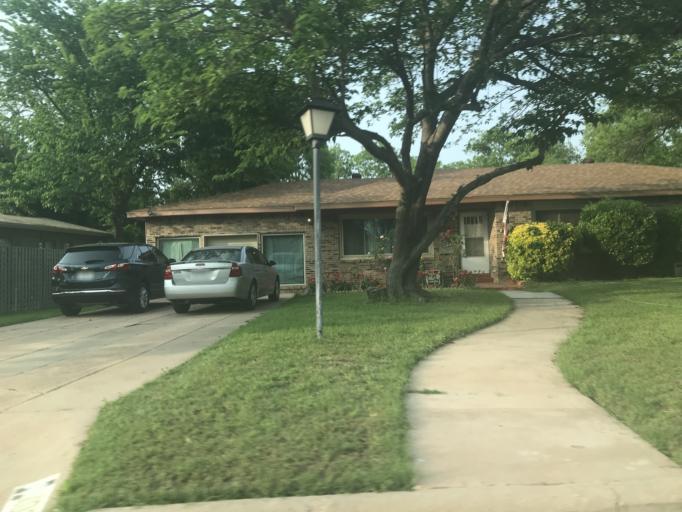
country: US
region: Texas
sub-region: Taylor County
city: Abilene
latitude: 32.4381
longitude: -99.7744
